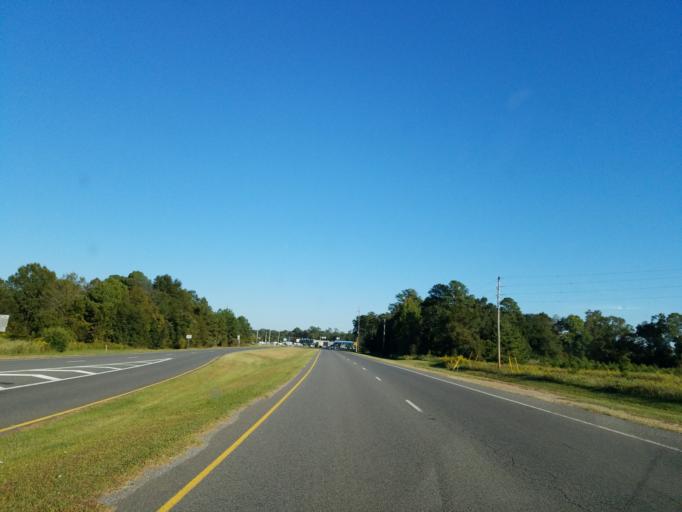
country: US
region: Georgia
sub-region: Lee County
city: Leesburg
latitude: 31.7217
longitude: -84.1768
